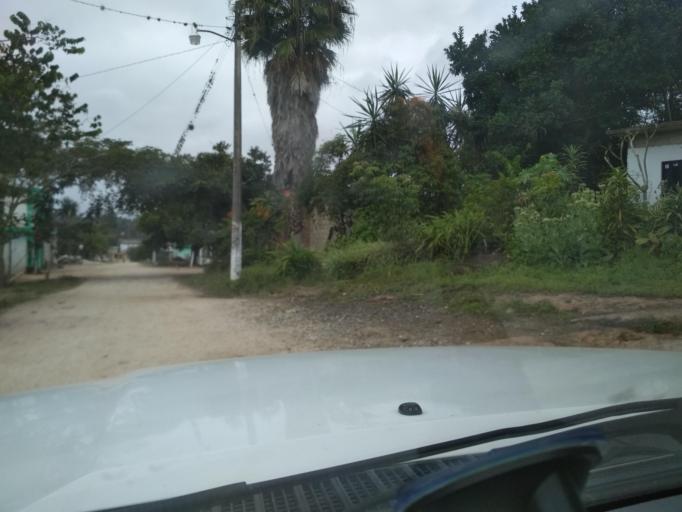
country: MX
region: Veracruz
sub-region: Emiliano Zapata
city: Dos Rios
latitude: 19.5371
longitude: -96.7952
